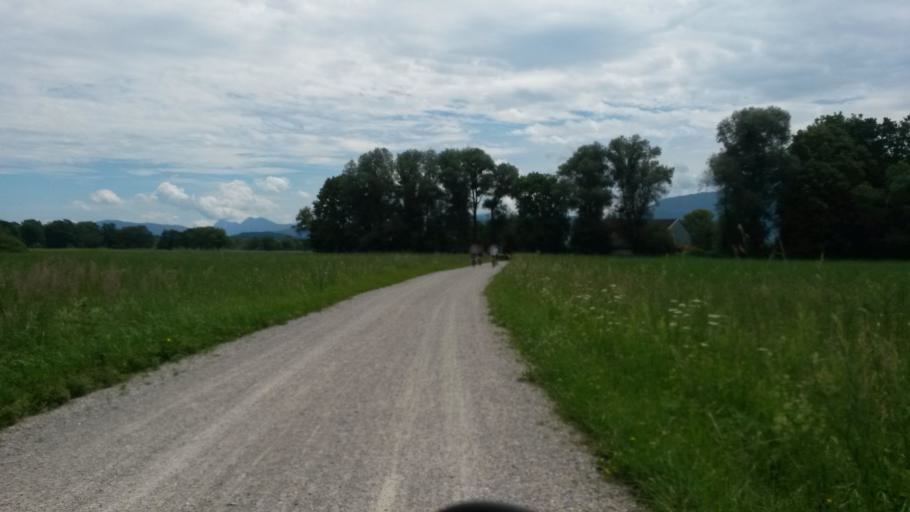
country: DE
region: Bavaria
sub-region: Upper Bavaria
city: Ubersee
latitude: 47.8557
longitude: 12.4855
